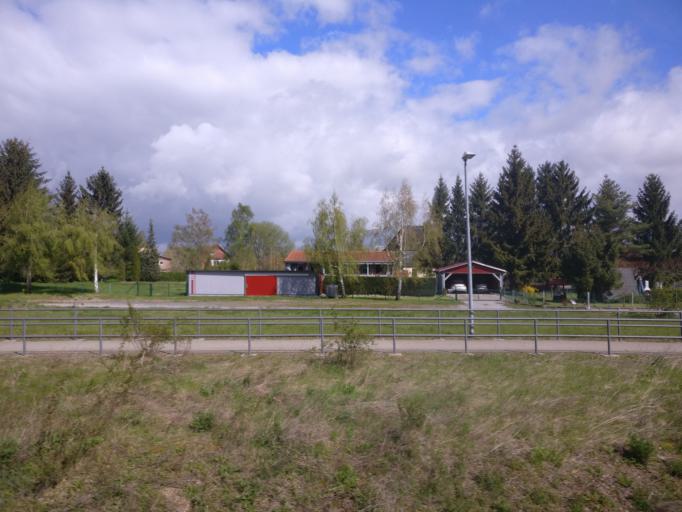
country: DE
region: Saxony-Anhalt
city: Heudeber
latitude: 51.9051
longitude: 10.8637
